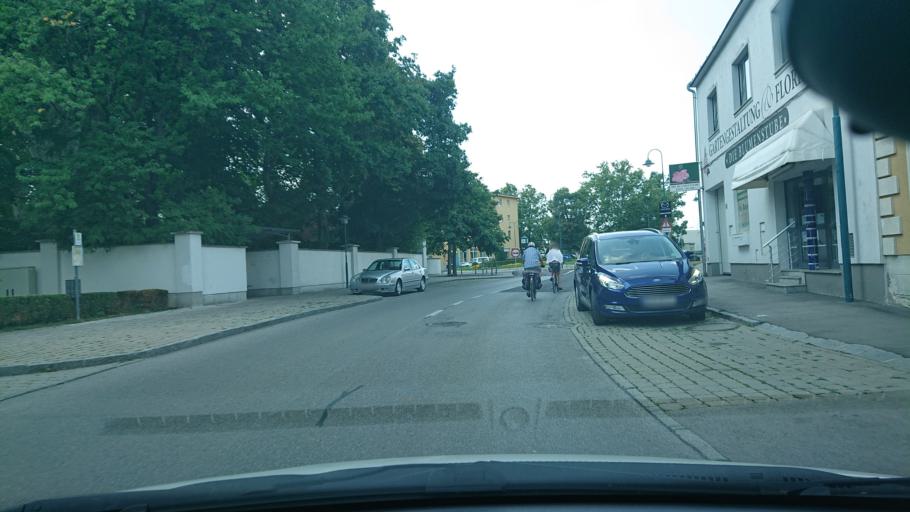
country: AT
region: Lower Austria
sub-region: Politischer Bezirk Baden
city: Kottingbrunn
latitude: 47.9518
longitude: 16.2288
